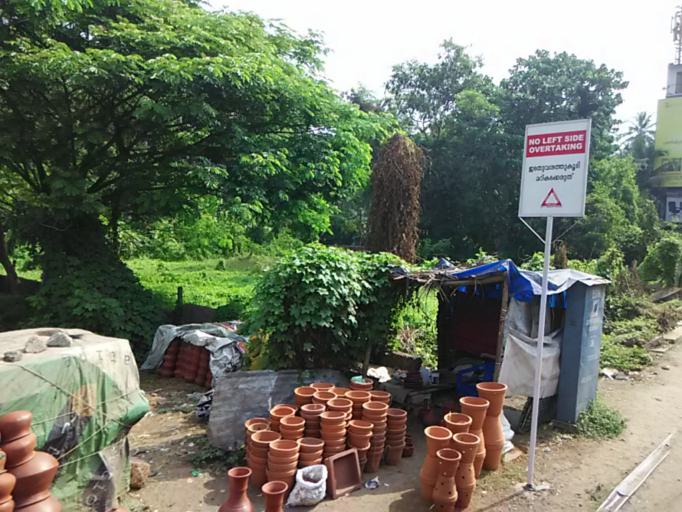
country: IN
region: Kerala
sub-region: Kozhikode
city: Kozhikode
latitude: 11.2584
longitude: 75.7964
